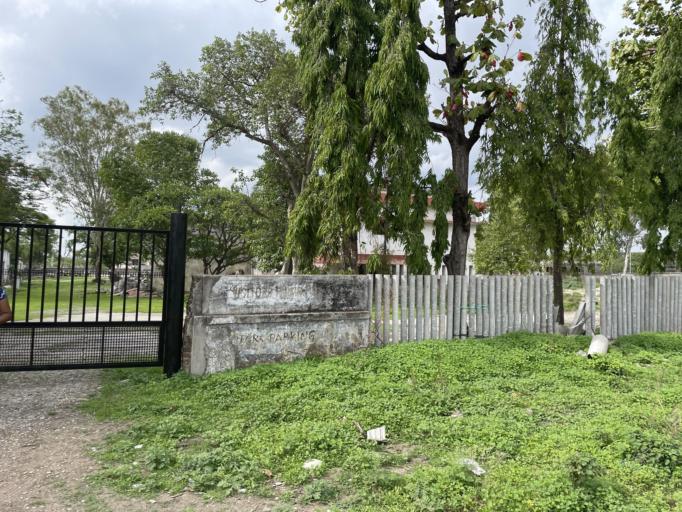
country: IN
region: Maharashtra
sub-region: Aurangabad Division
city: Aurangabad
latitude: 19.8826
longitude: 75.3794
